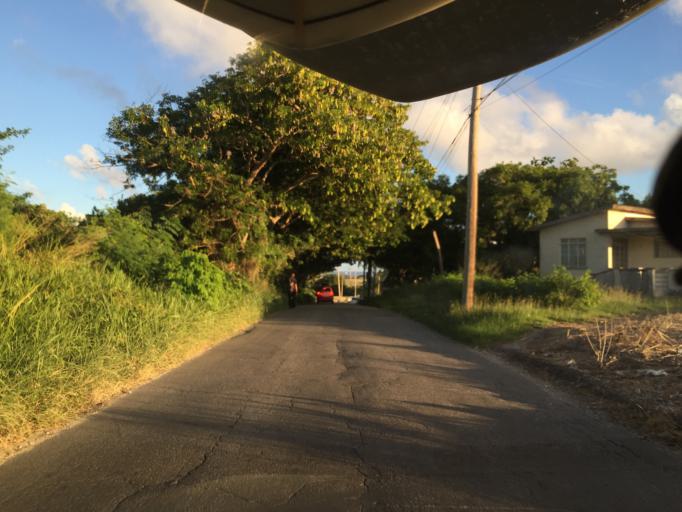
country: BB
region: Christ Church
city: Oistins
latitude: 13.0761
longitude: -59.5132
